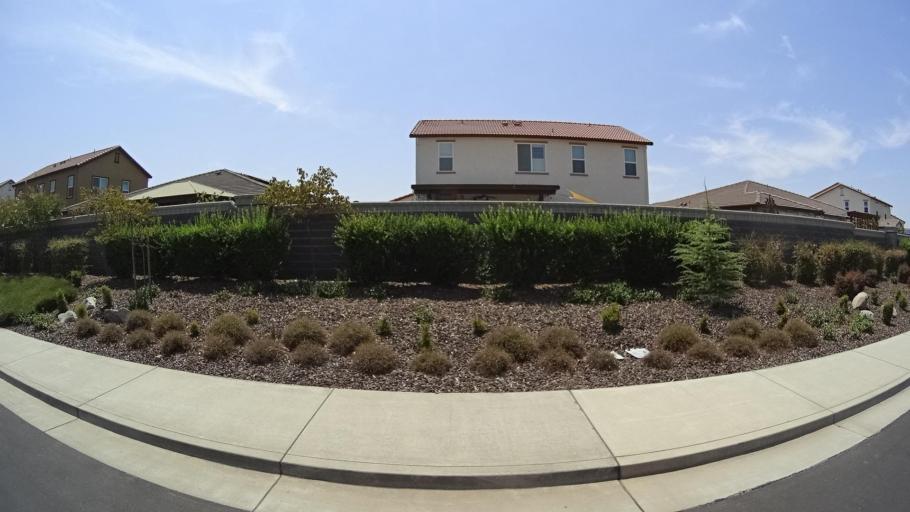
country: US
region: California
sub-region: Placer County
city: Rocklin
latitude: 38.8062
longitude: -121.2206
